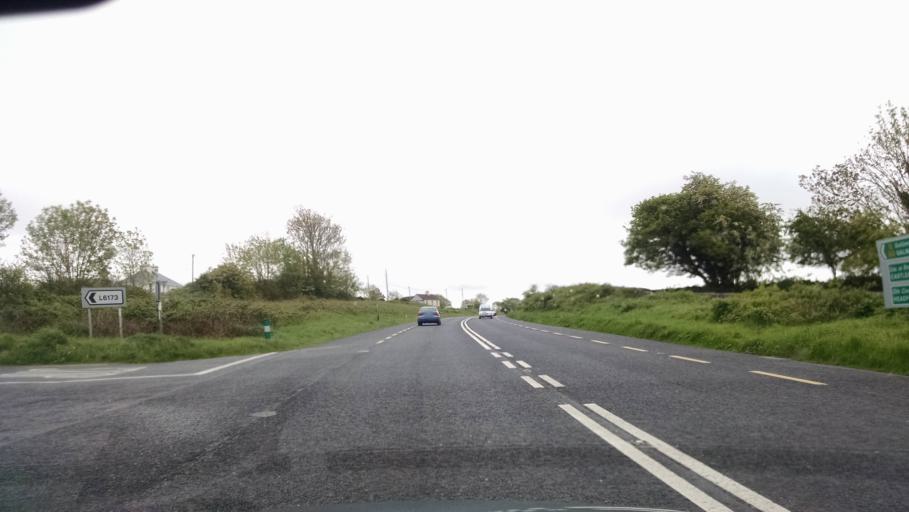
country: IE
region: Connaught
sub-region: County Galway
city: Claregalway
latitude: 53.4104
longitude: -9.0188
